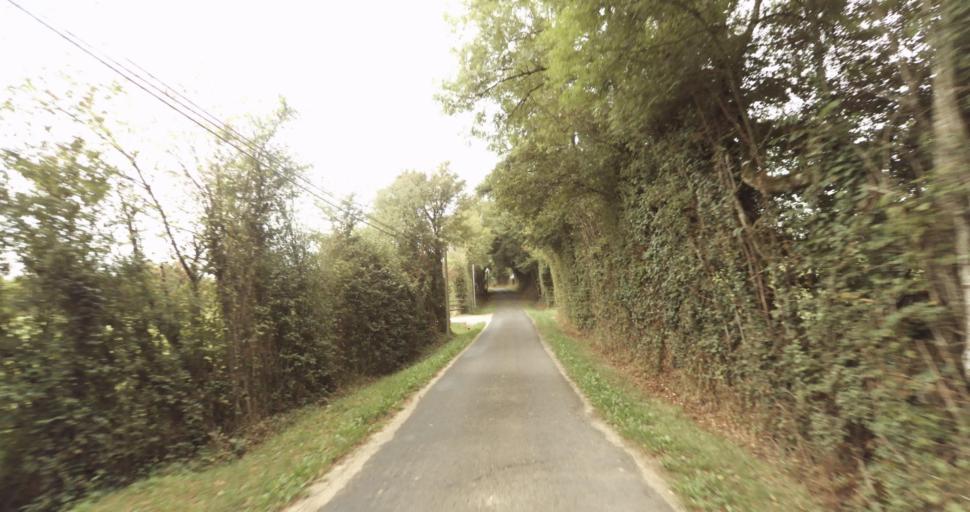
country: FR
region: Lower Normandy
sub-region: Departement de l'Orne
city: Gace
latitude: 48.7307
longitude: 0.2930
